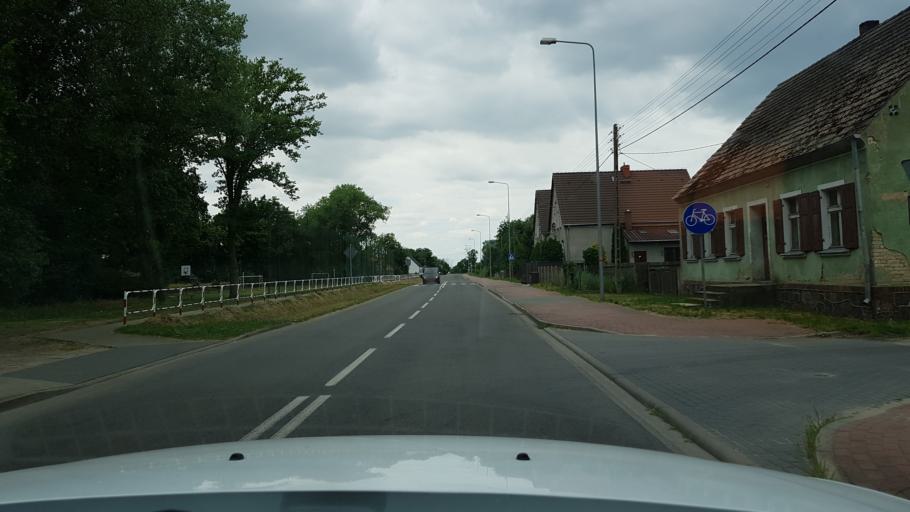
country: PL
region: Lubusz
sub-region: Powiat gorzowski
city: Kostrzyn nad Odra
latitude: 52.6230
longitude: 14.5827
